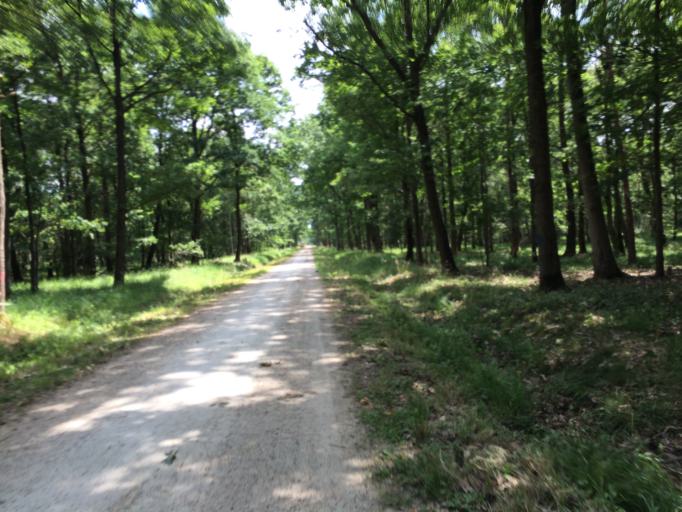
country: FR
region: Ile-de-France
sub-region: Departement de l'Essonne
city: Epinay-sous-Senart
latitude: 48.6688
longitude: 2.4994
